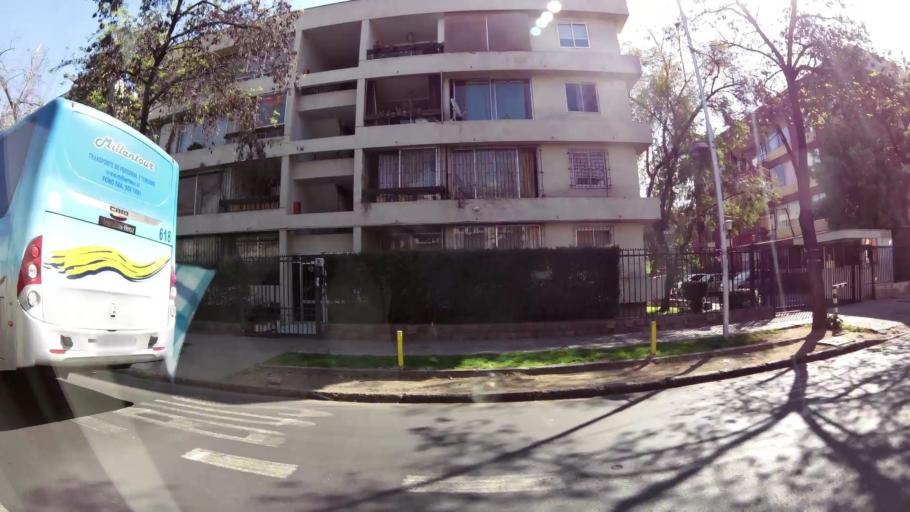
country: CL
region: Santiago Metropolitan
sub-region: Provincia de Santiago
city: Santiago
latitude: -33.4340
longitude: -70.6388
